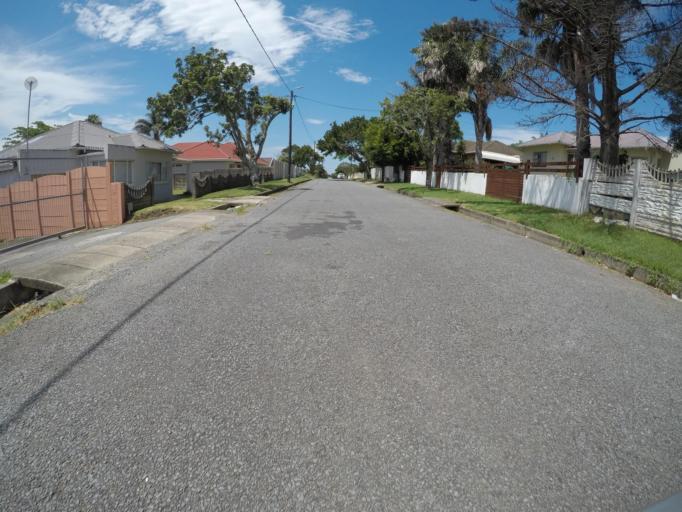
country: ZA
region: Eastern Cape
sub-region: Buffalo City Metropolitan Municipality
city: East London
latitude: -33.0333
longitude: 27.8580
